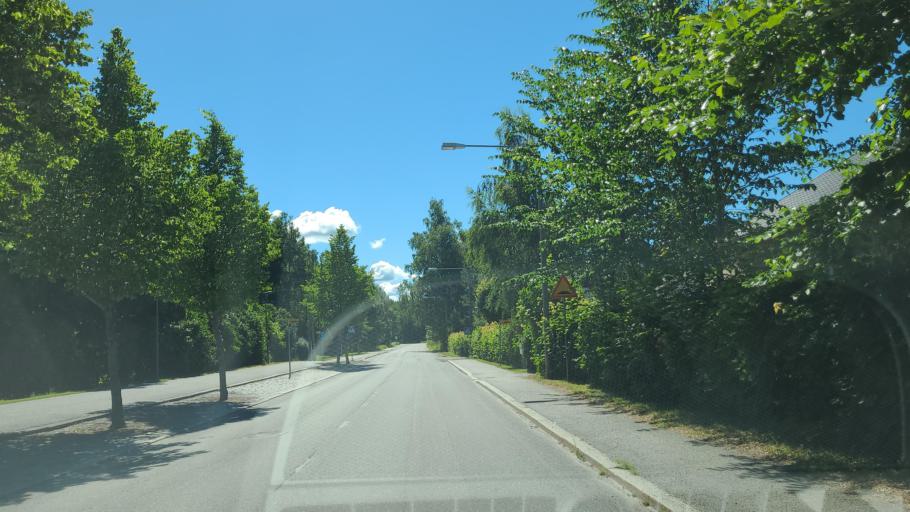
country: FI
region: Ostrobothnia
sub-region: Vaasa
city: Ristinummi
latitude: 63.0711
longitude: 21.7232
